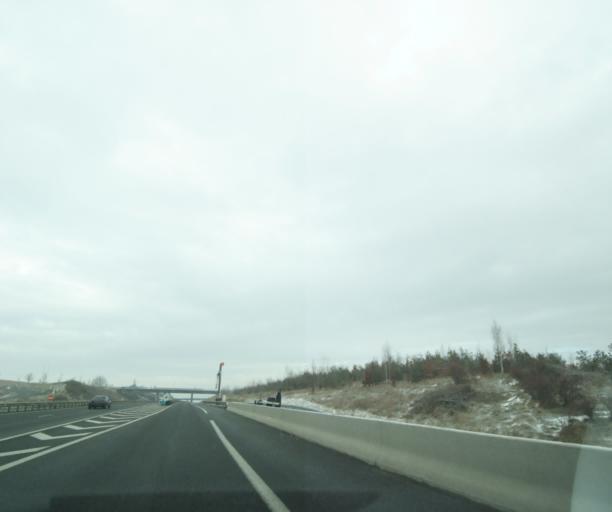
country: FR
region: Auvergne
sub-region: Departement du Puy-de-Dome
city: Combronde
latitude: 45.9699
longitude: 3.1003
